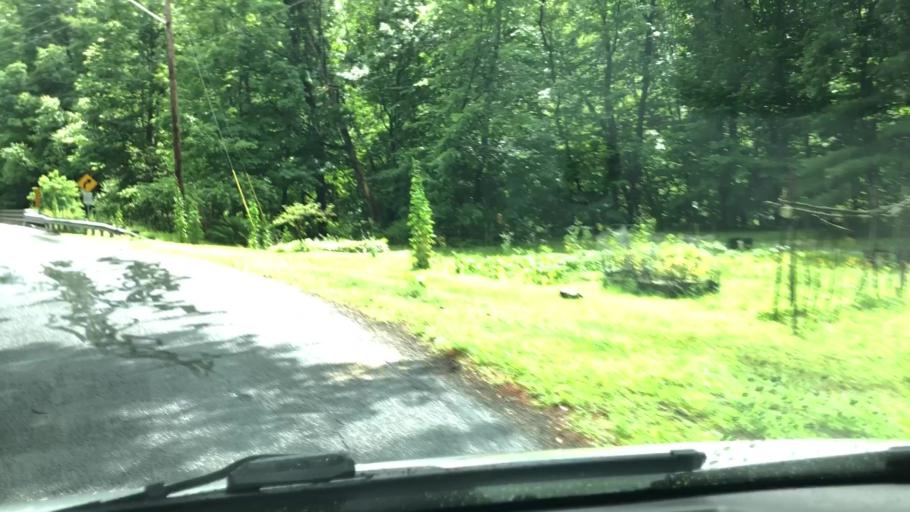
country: US
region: Massachusetts
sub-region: Hampshire County
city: Williamsburg
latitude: 42.3675
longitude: -72.7026
